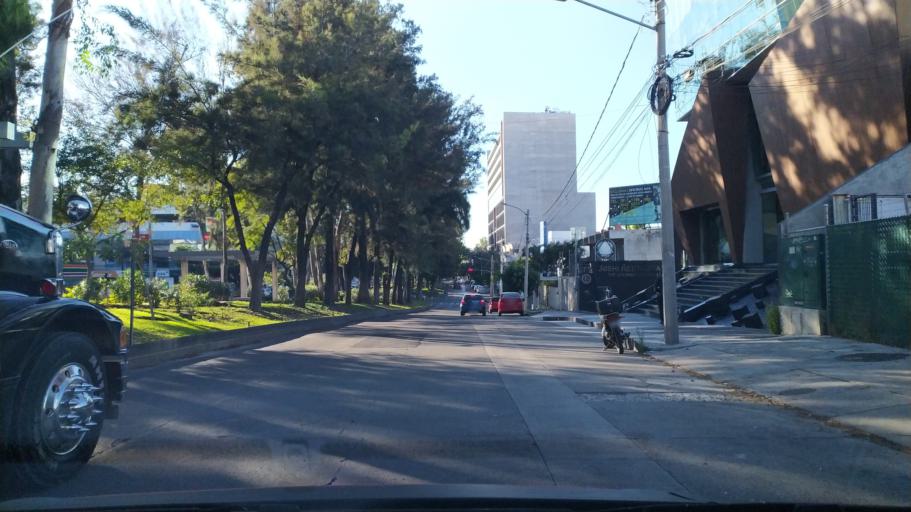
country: MX
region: Jalisco
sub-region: Zapopan
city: Zapopan
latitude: 20.6975
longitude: -103.3817
